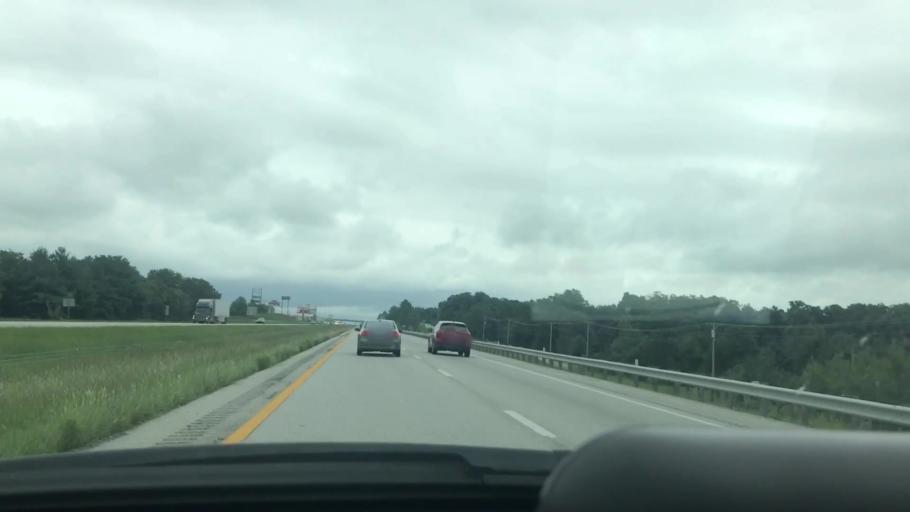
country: US
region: Missouri
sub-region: Jasper County
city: Duquesne
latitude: 37.0503
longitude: -94.4596
